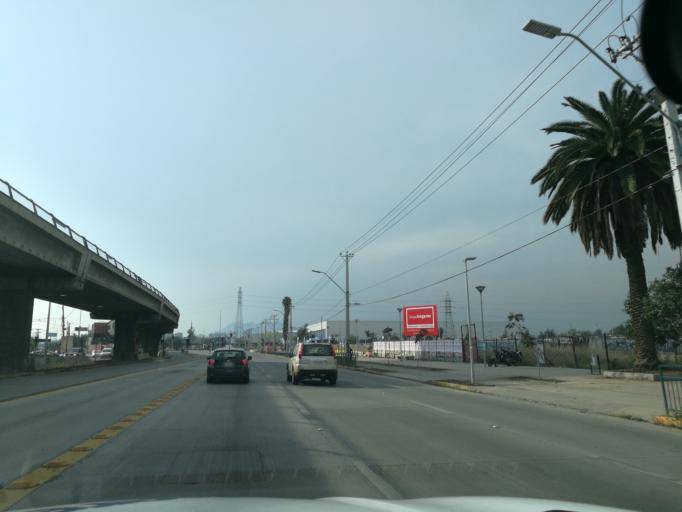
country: CL
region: Santiago Metropolitan
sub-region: Provincia de Santiago
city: Santiago
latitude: -33.4887
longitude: -70.6180
